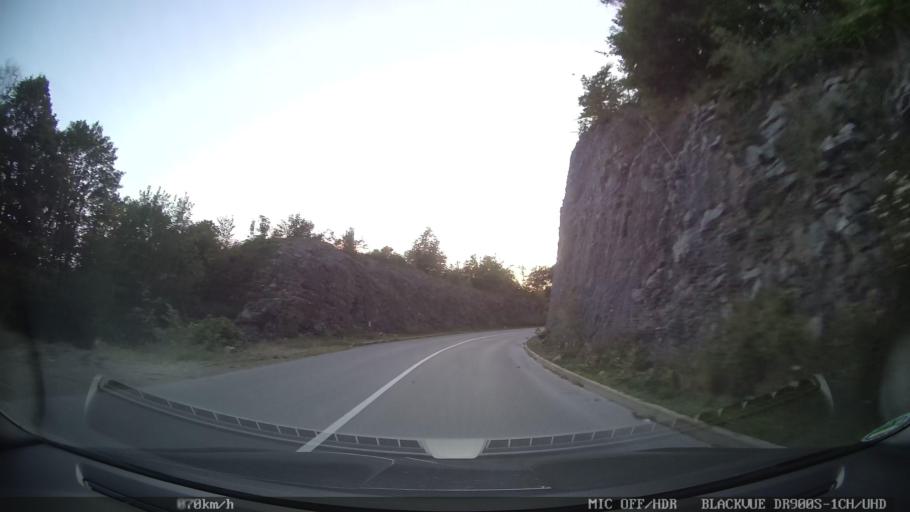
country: HR
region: Primorsko-Goranska
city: Novi Vinodolski
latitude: 45.1624
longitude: 14.9508
